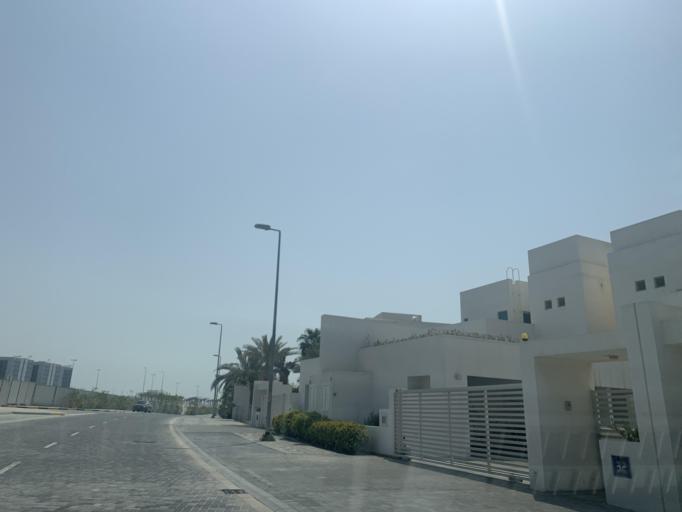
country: BH
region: Muharraq
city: Al Hadd
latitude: 26.2740
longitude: 50.6710
